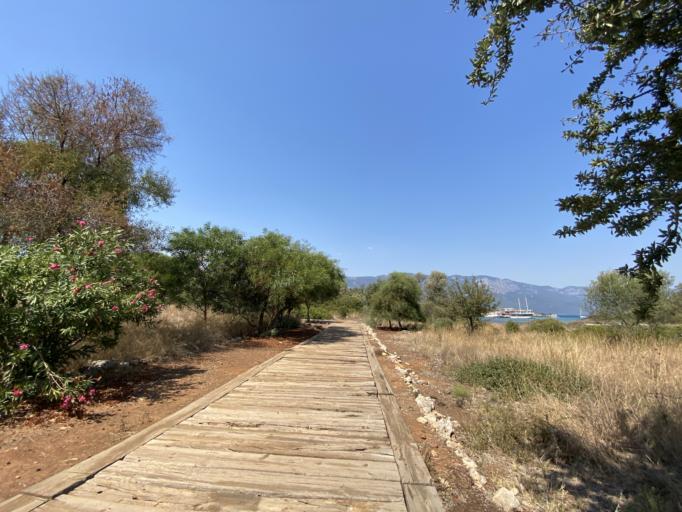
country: TR
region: Mugla
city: Yerkesik
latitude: 36.9917
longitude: 28.2040
